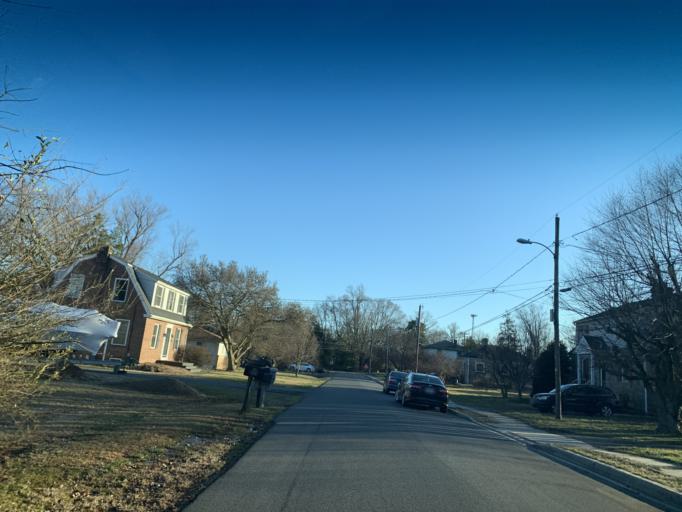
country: US
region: Maryland
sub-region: Cecil County
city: Perryville
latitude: 39.5627
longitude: -76.0685
